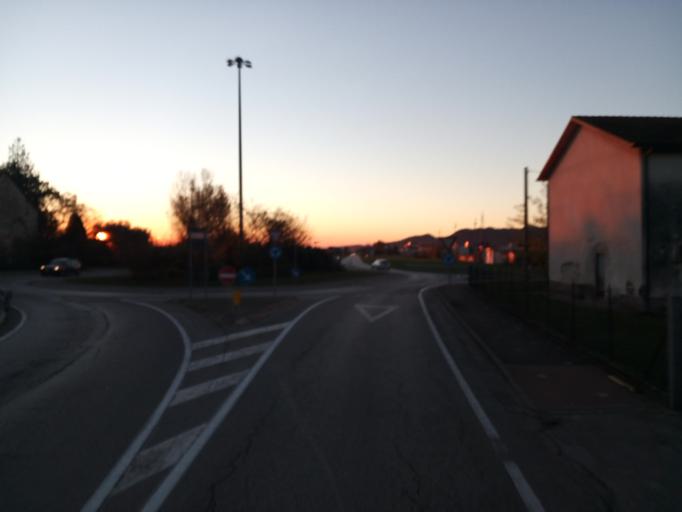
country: IT
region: Veneto
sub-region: Provincia di Vicenza
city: San Vito di Leguzzano
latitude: 45.6954
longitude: 11.3704
